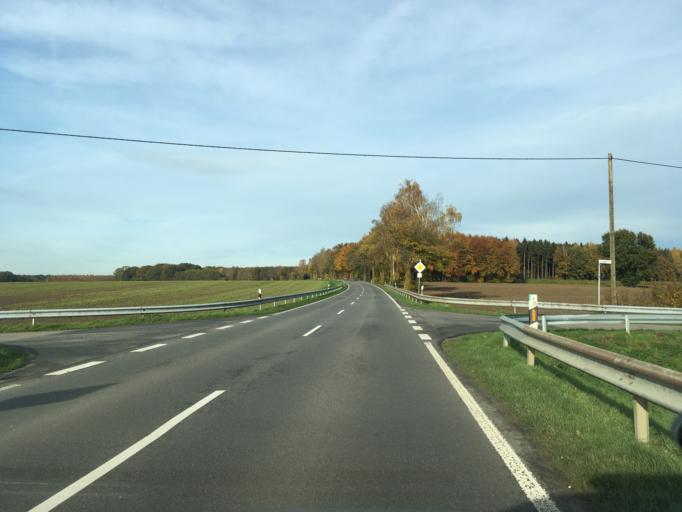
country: DE
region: North Rhine-Westphalia
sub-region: Regierungsbezirk Munster
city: Heiden
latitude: 51.8381
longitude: 6.9333
